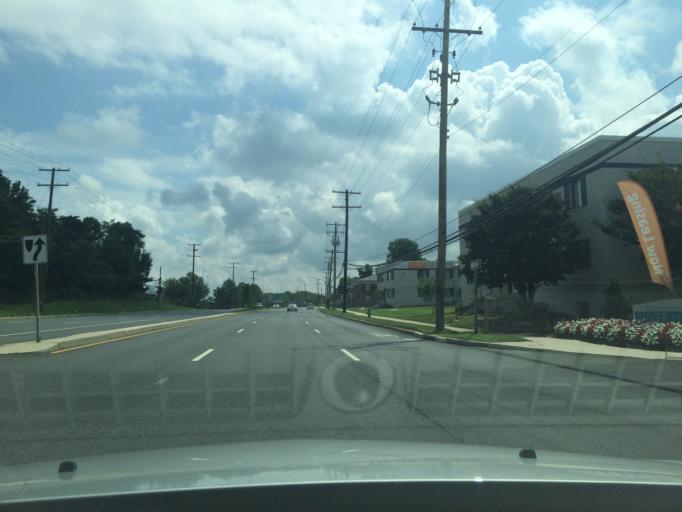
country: US
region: Maryland
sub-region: Prince George's County
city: Silver Hill
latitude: 38.8422
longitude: -76.9360
